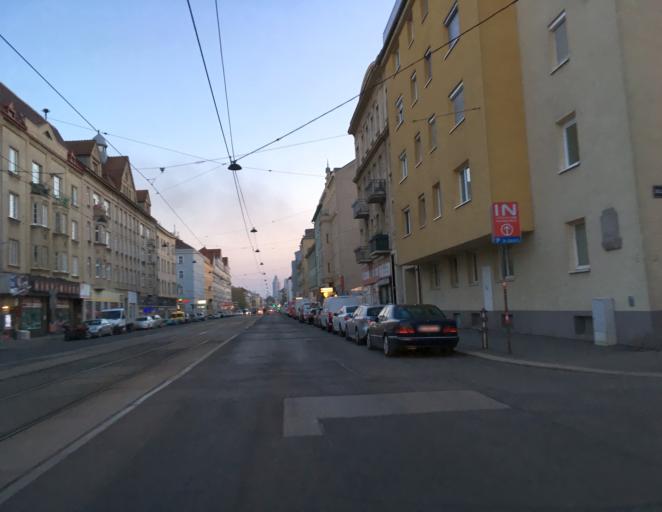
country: AT
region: Lower Austria
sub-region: Politischer Bezirk Korneuburg
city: Langenzersdorf
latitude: 48.2642
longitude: 16.4015
